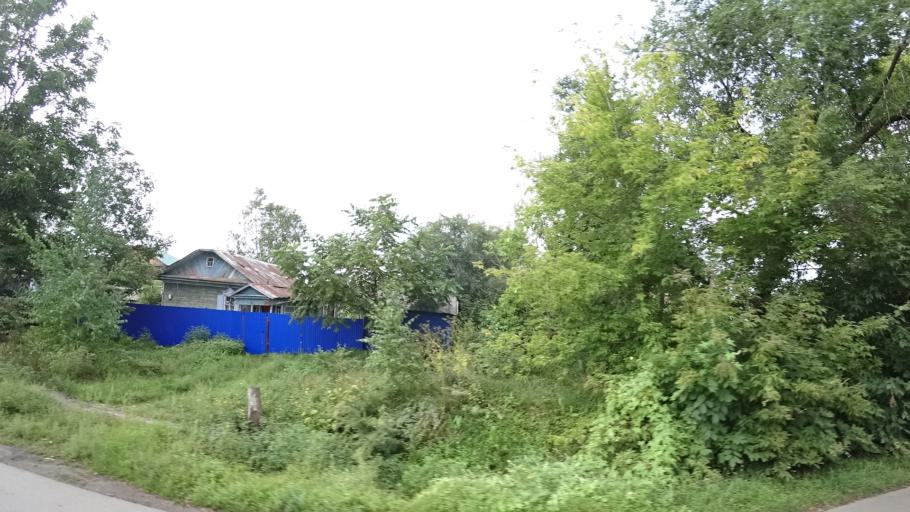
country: RU
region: Primorskiy
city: Chernigovka
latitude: 44.3442
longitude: 132.5652
